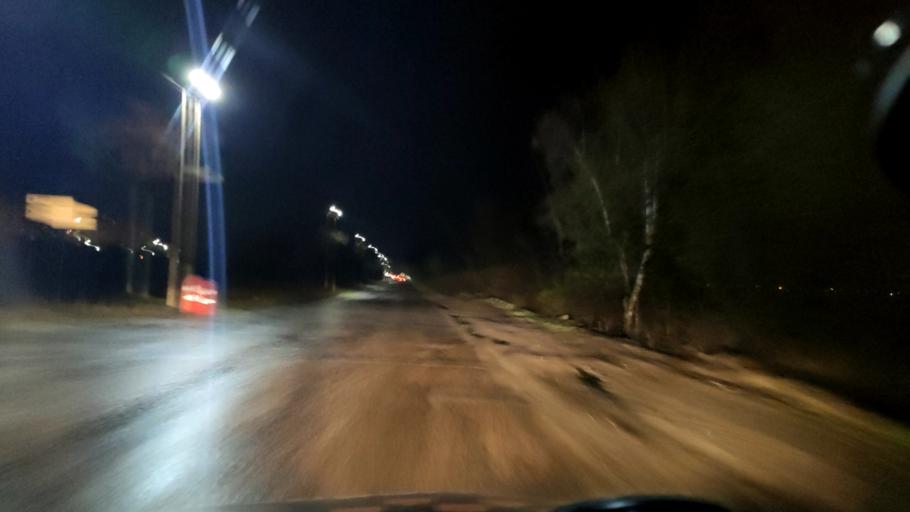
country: RU
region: Voronezj
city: Novaya Usman'
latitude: 51.6537
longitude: 39.3290
